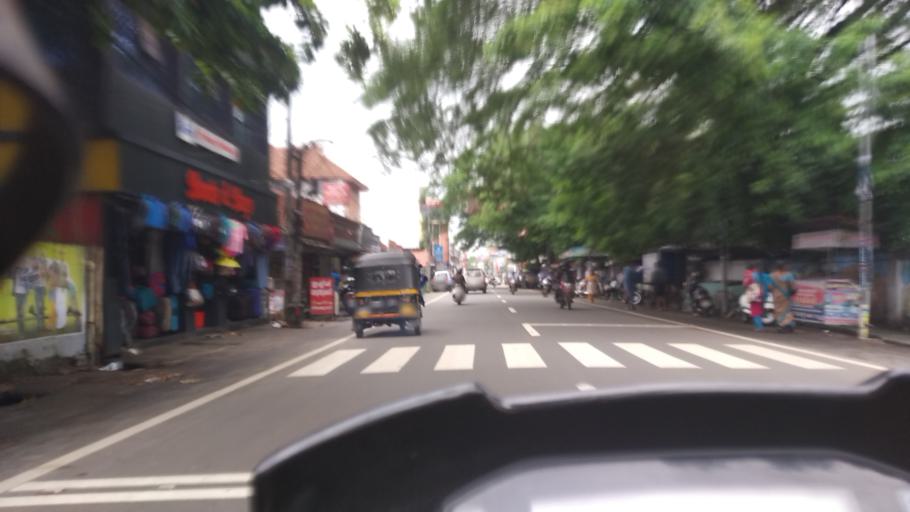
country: IN
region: Kerala
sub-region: Alappuzha
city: Alleppey
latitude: 9.4926
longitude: 76.3387
